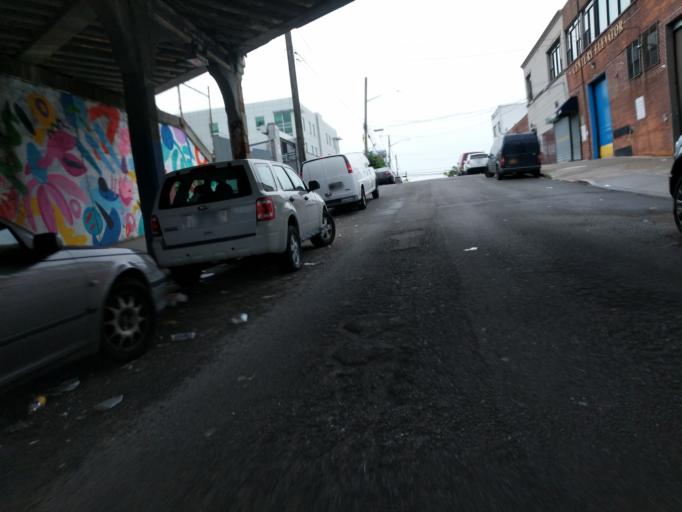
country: US
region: New York
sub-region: Queens County
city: Long Island City
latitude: 40.7637
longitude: -73.9052
